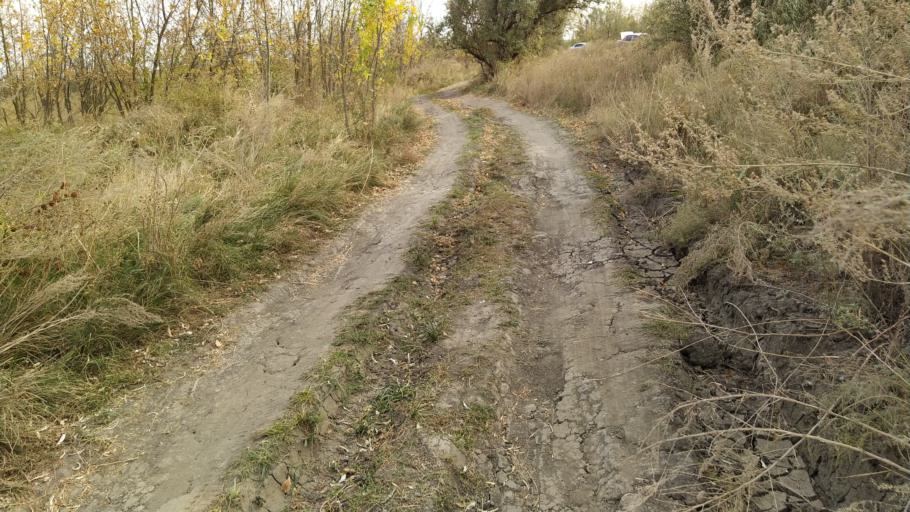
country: RU
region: Rostov
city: Kuleshovka
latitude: 47.1360
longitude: 39.5806
